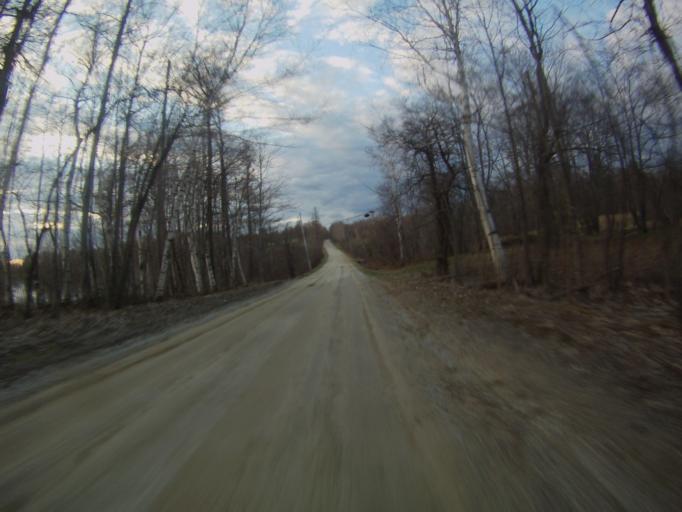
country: US
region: Vermont
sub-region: Rutland County
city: Brandon
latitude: 43.8941
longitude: -73.0120
